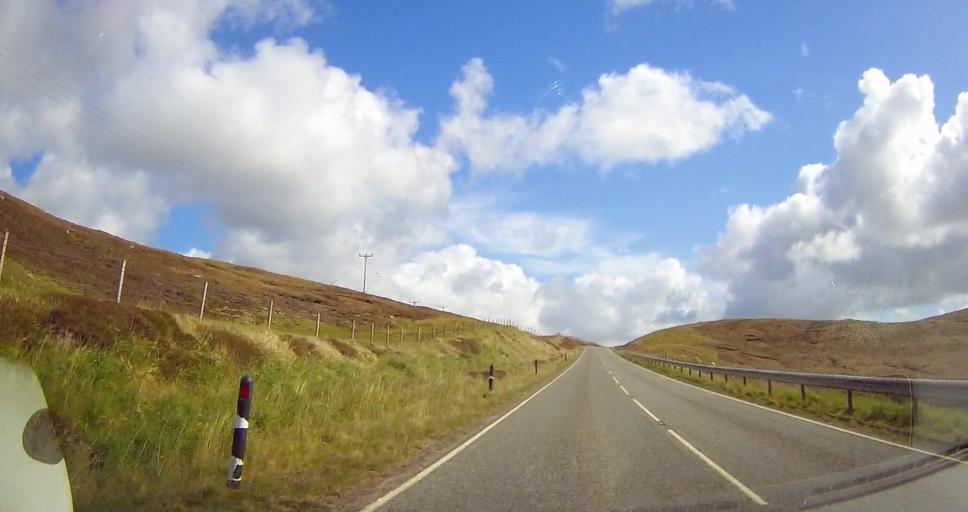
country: GB
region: Scotland
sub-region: Shetland Islands
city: Lerwick
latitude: 60.4576
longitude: -1.3990
